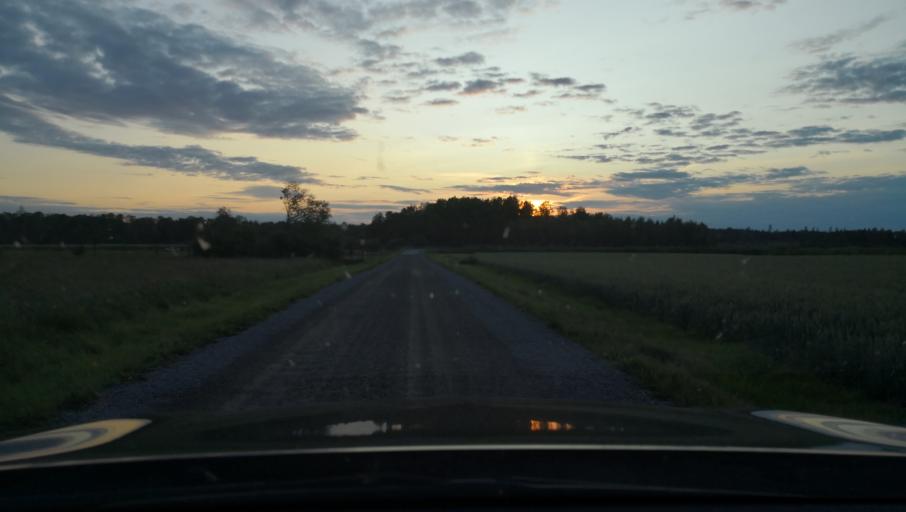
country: SE
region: Uppsala
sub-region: Osthammars Kommun
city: Bjorklinge
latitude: 60.0596
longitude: 17.5844
